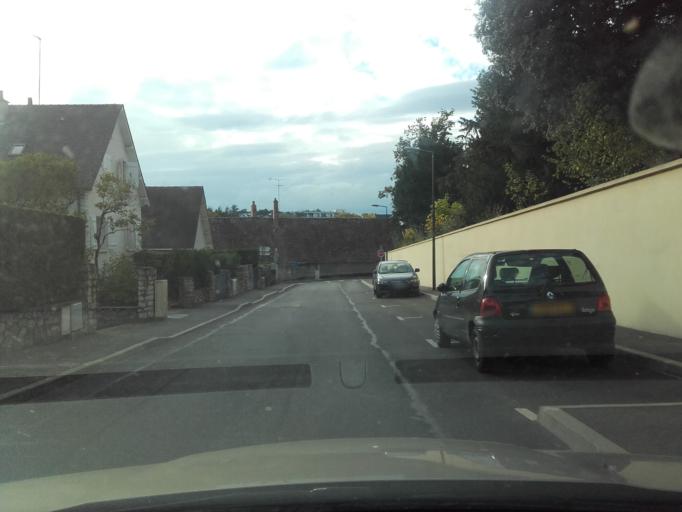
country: FR
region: Centre
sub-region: Departement d'Indre-et-Loire
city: Saint-Cyr-sur-Loire
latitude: 47.4063
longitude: 0.6871
